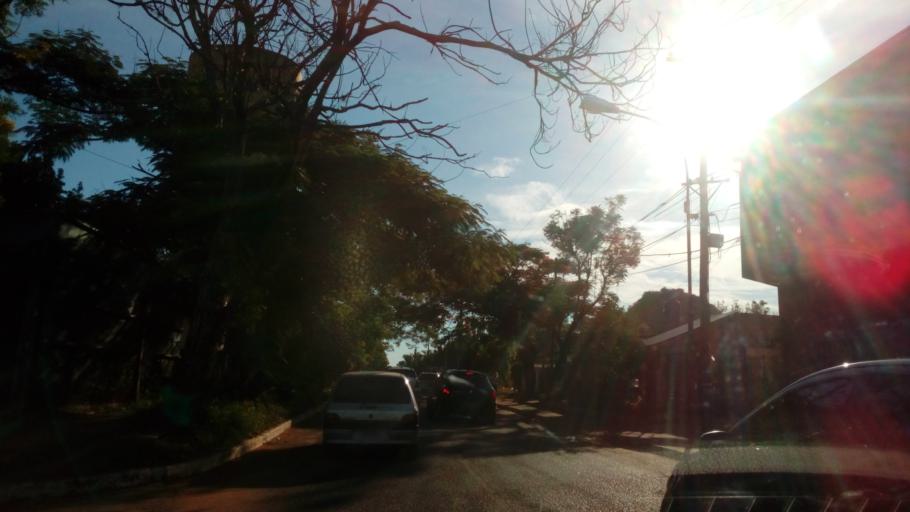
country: AR
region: Misiones
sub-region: Departamento de Capital
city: Posadas
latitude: -27.4300
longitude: -55.8821
